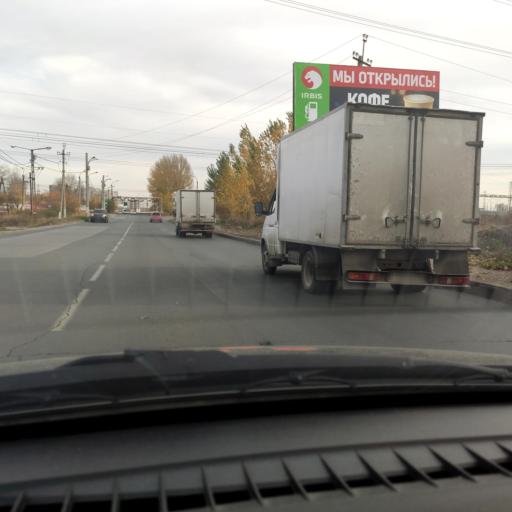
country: RU
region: Samara
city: Zhigulevsk
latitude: 53.4872
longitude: 49.5068
